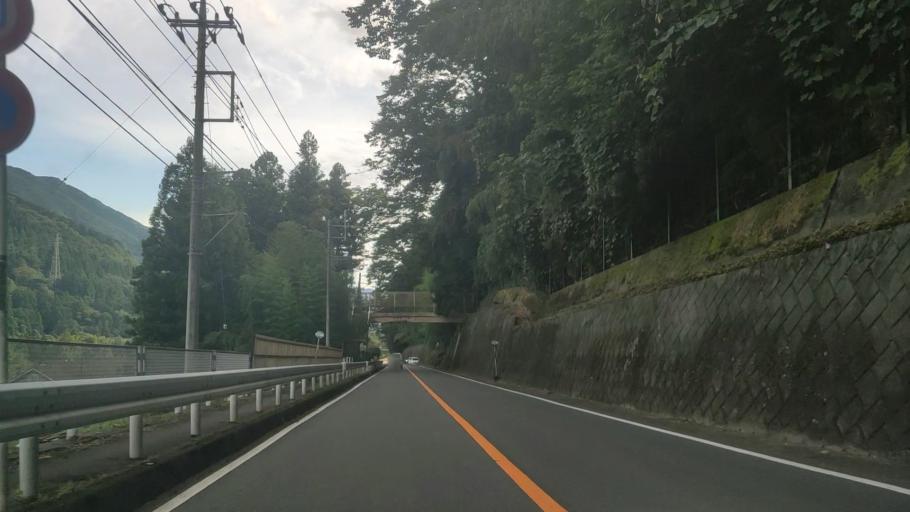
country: JP
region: Gunma
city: Omamacho-omama
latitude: 36.5380
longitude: 139.3397
